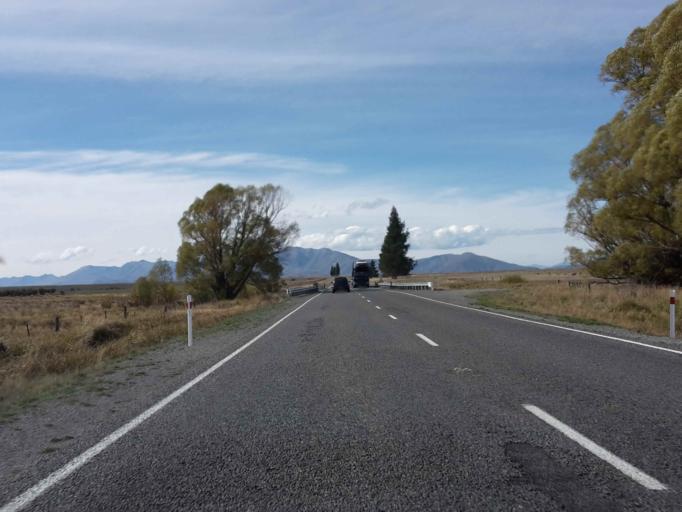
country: NZ
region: Canterbury
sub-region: Timaru District
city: Pleasant Point
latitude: -44.1755
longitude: 170.3218
